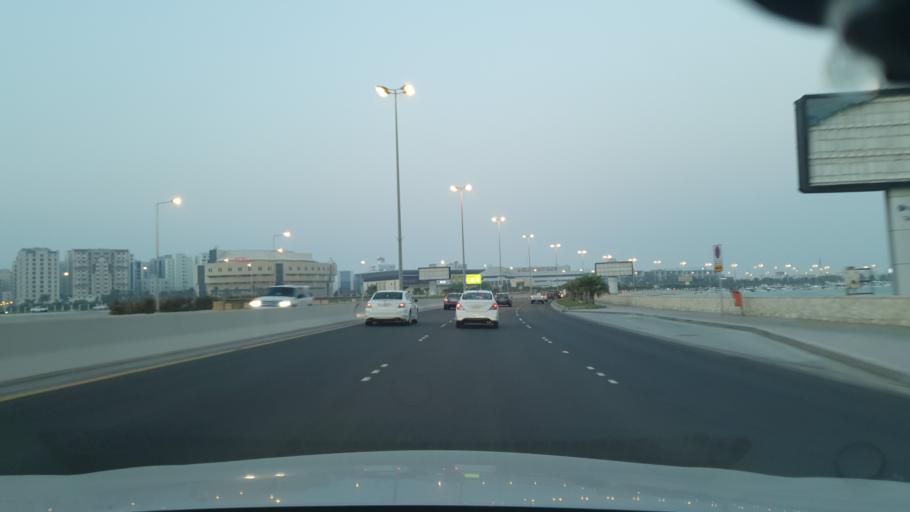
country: BH
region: Muharraq
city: Al Muharraq
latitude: 26.2575
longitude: 50.5952
